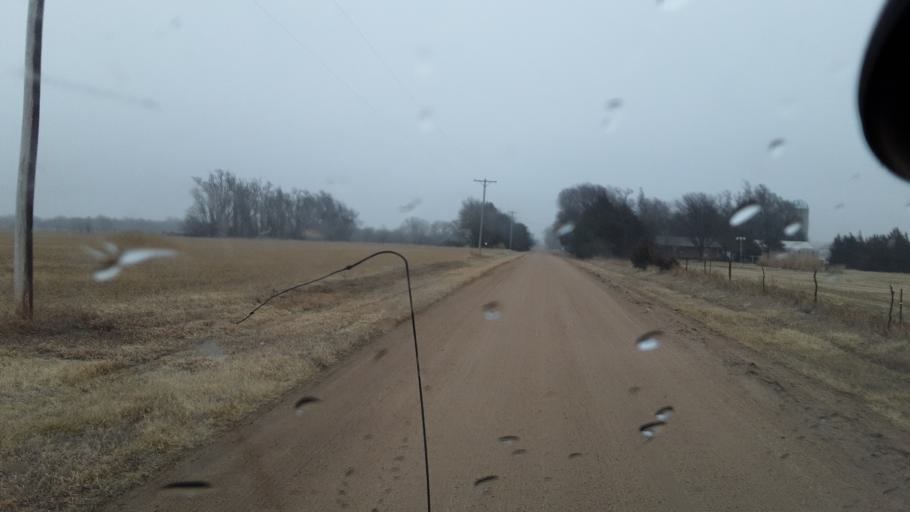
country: US
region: Kansas
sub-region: Reno County
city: South Hutchinson
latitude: 37.9555
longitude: -98.0298
